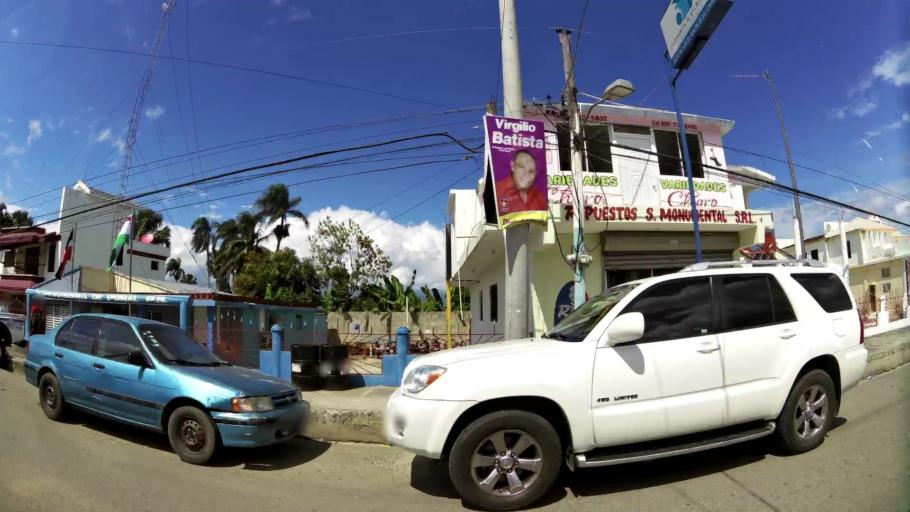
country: DO
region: Santiago
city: Licey al Medio
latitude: 19.3801
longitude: -70.6154
